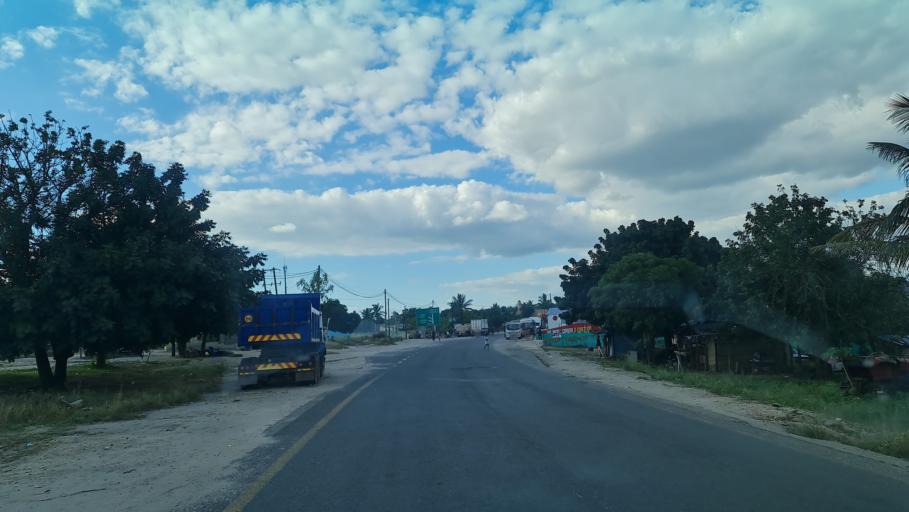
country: MZ
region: Manica
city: Chimoio
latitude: -19.2129
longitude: 33.9241
